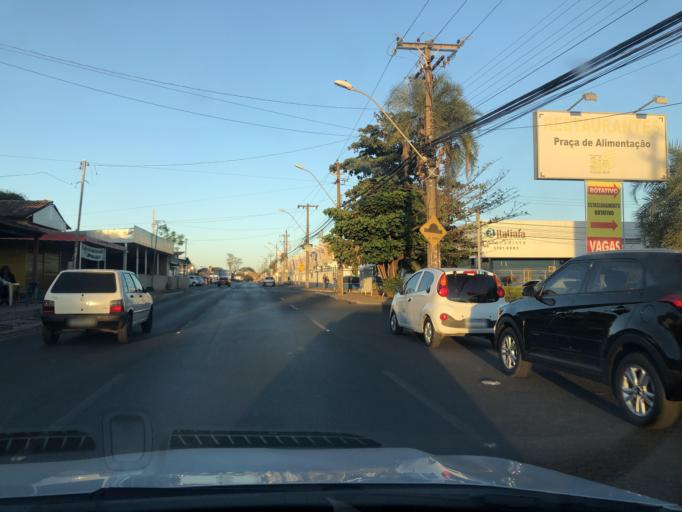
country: BR
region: Federal District
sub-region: Brasilia
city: Brasilia
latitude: -15.8022
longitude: -47.9570
